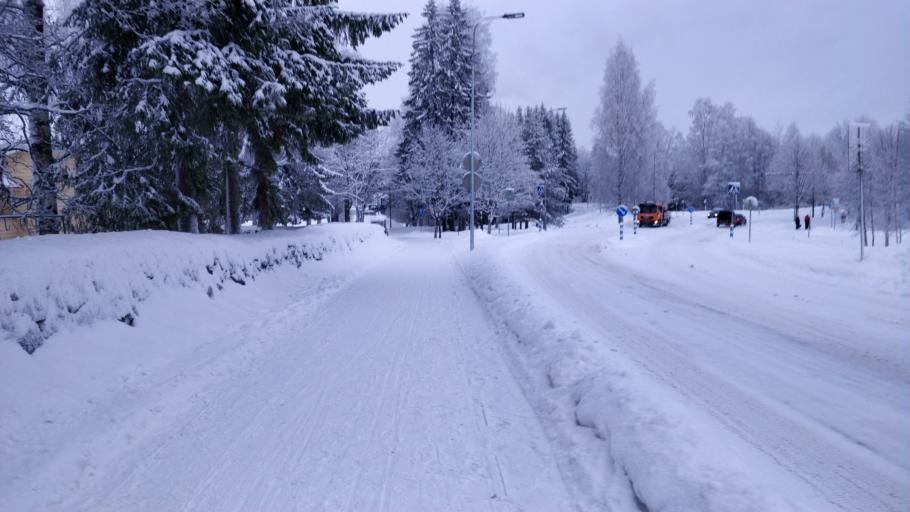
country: FI
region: Southern Savonia
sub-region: Mikkeli
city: Puumala
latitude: 61.5243
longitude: 28.1778
